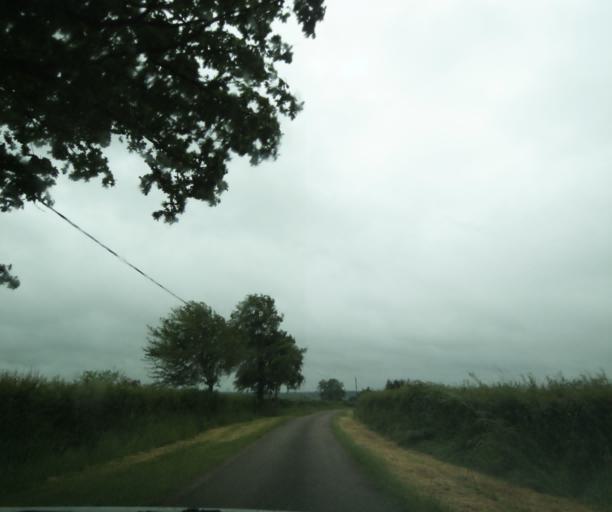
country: FR
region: Bourgogne
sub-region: Departement de Saone-et-Loire
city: Palinges
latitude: 46.4955
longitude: 4.1941
